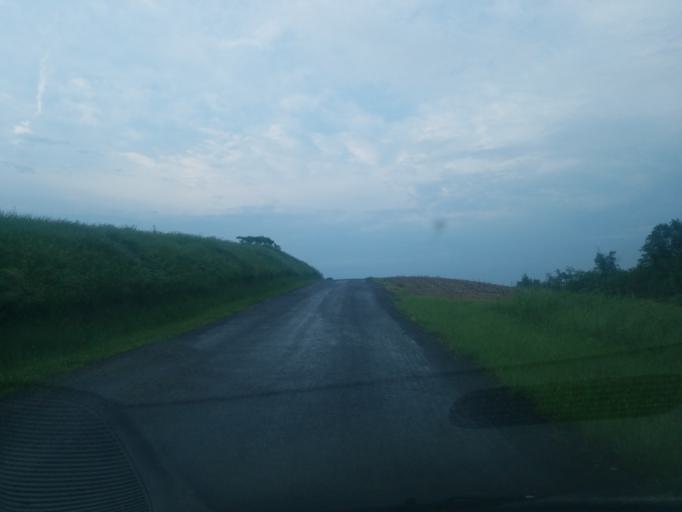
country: US
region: Ohio
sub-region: Stark County
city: Minerva
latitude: 40.7599
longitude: -80.9511
